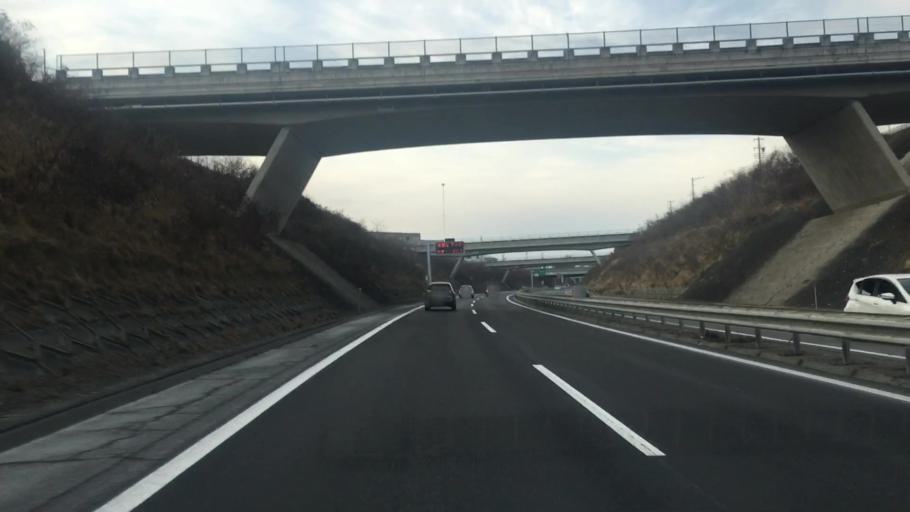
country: JP
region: Nagano
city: Komoro
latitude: 36.2826
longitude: 138.4878
